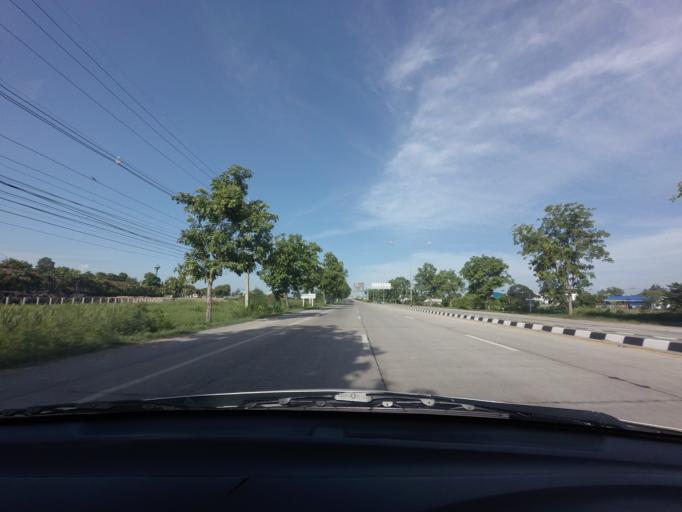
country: TH
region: Suphan Buri
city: Suphan Buri
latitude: 14.4456
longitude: 100.1273
